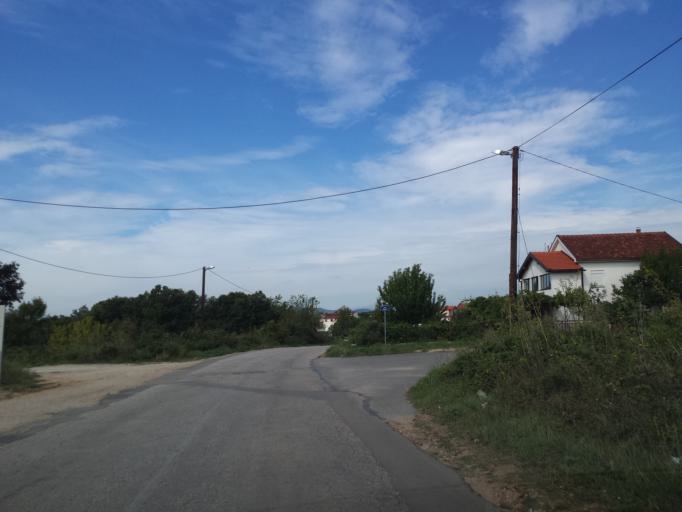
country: BA
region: Federation of Bosnia and Herzegovina
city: Citluk
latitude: 43.1974
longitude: 17.6679
